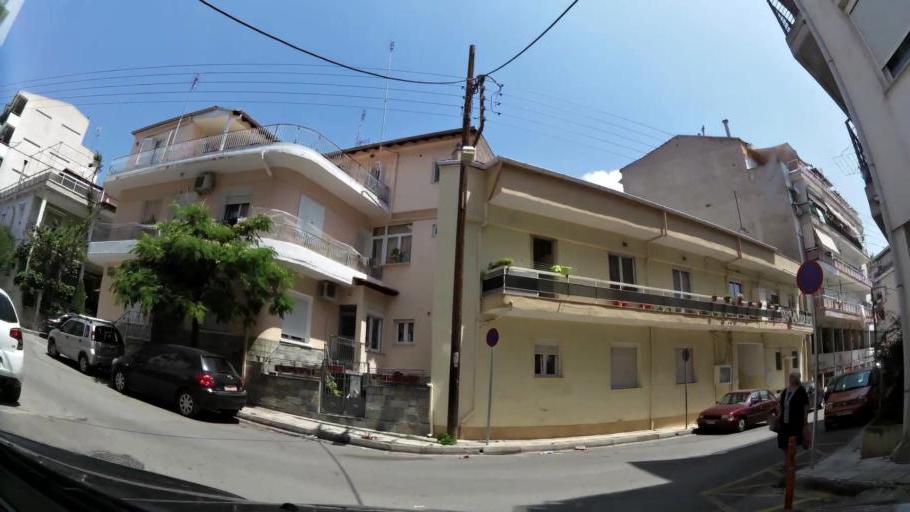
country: GR
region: West Macedonia
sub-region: Nomos Kozanis
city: Kozani
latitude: 40.2988
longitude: 21.7842
